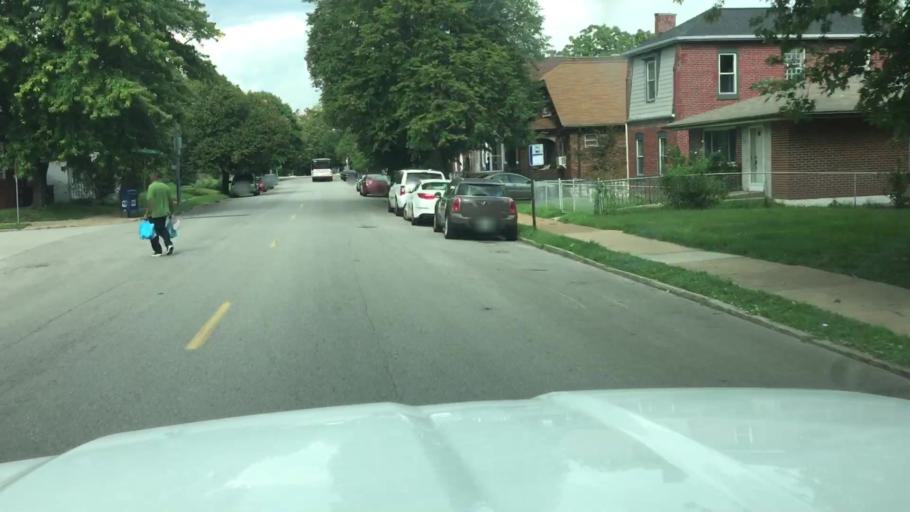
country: US
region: Missouri
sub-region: Saint Louis County
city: Lemay
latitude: 38.5609
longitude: -90.2474
